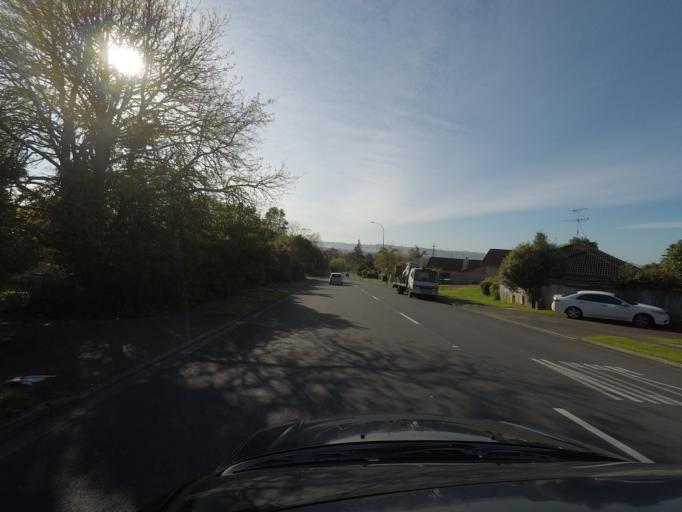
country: NZ
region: Auckland
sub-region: Auckland
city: Takanini
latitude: -37.0134
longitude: 174.9173
